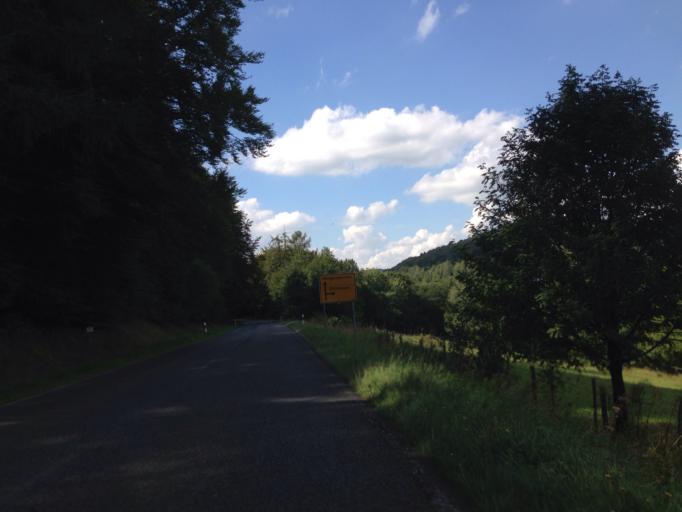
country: DE
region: Hesse
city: Merenberg
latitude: 50.5395
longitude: 8.2241
